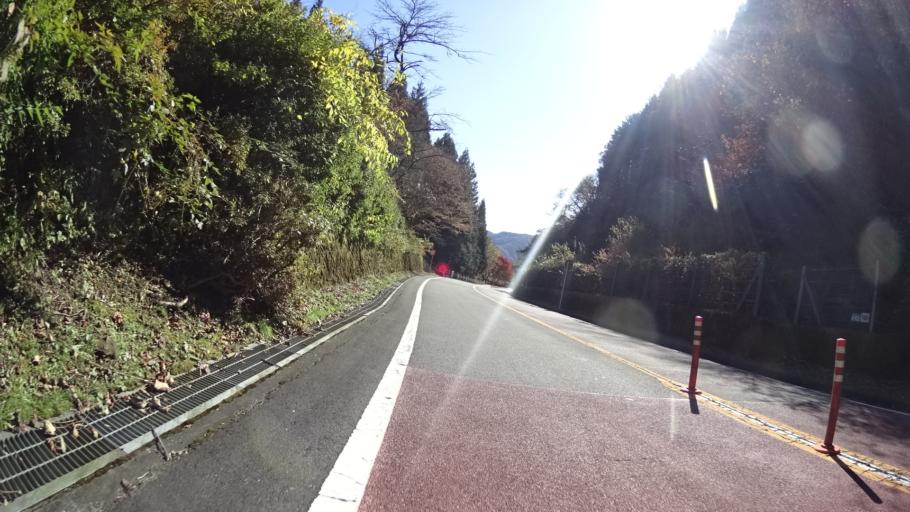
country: JP
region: Yamanashi
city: Uenohara
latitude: 35.7399
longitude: 139.0383
